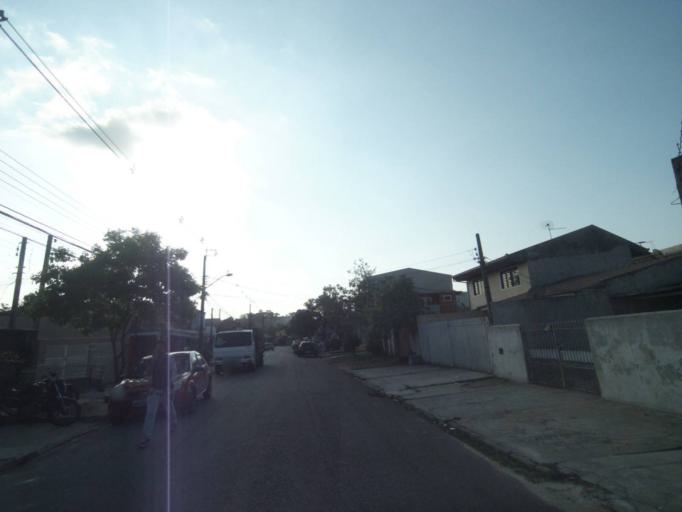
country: BR
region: Parana
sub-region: Curitiba
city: Curitiba
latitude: -25.4903
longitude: -49.3342
